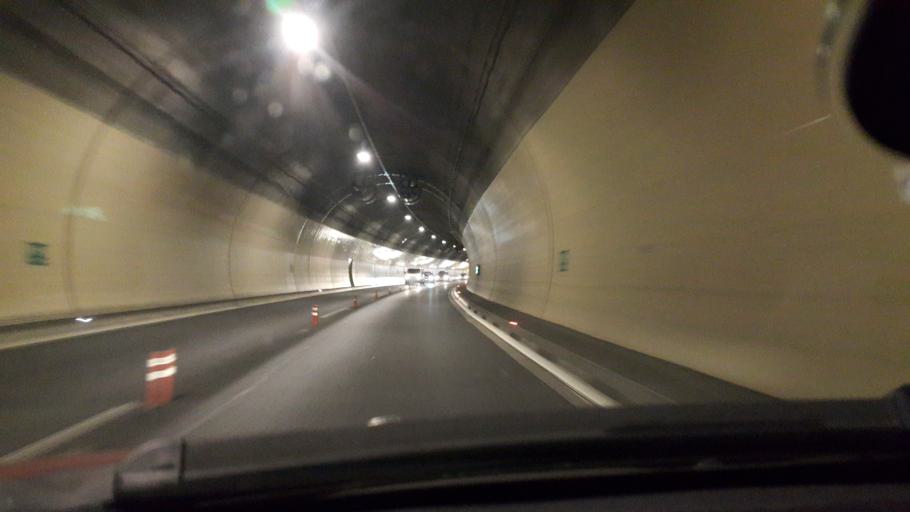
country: AT
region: Carinthia
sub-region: Klagenfurt am Woerthersee
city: Klagenfurt am Woerthersee
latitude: 46.6384
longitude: 14.2483
